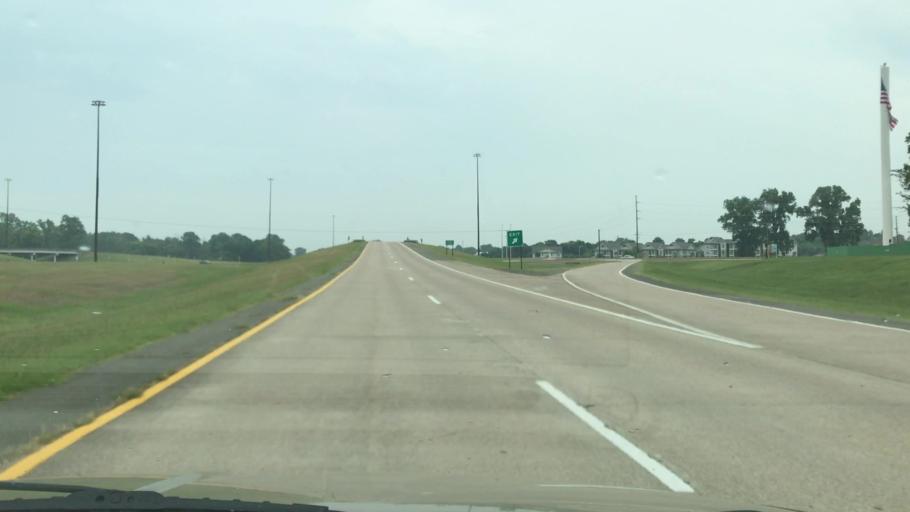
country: US
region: Louisiana
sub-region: Bossier Parish
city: Bossier City
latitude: 32.5021
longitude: -93.7180
